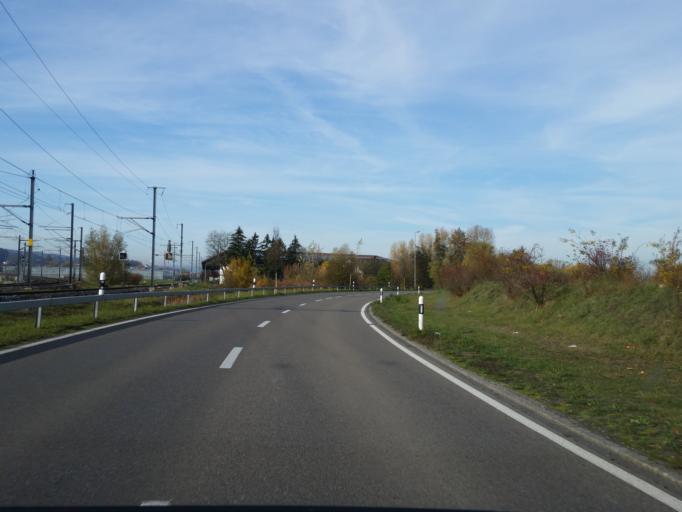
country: CH
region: Thurgau
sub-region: Kreuzlingen District
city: Gottlieben
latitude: 47.6574
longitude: 9.1483
